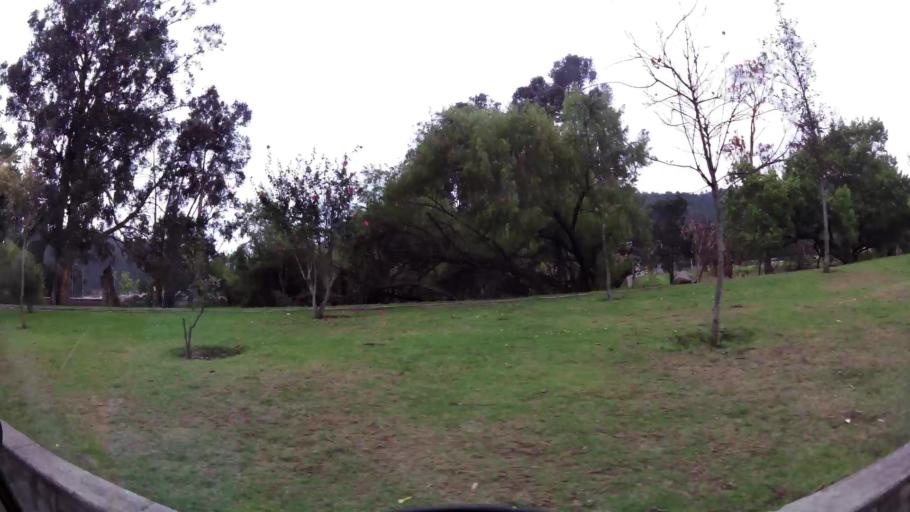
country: EC
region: Azuay
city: Cuenca
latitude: -2.9132
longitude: -78.9912
